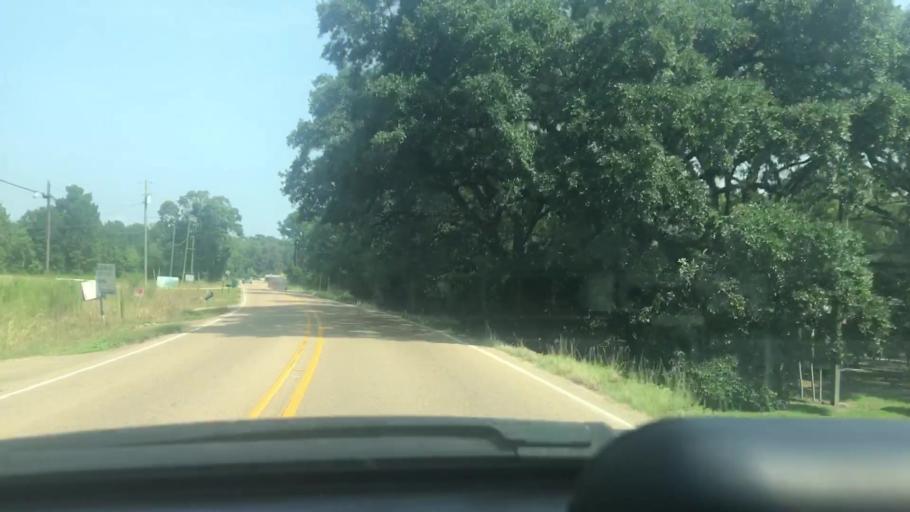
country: US
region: Louisiana
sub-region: Livingston Parish
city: Denham Springs
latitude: 30.4769
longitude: -90.9182
